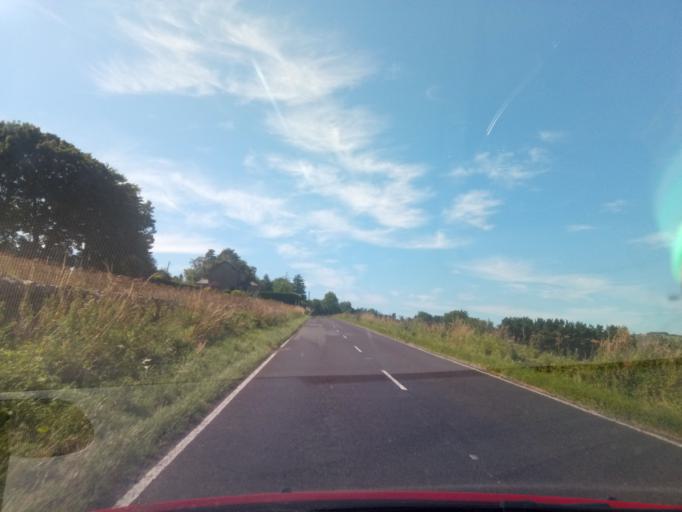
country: GB
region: England
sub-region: Northumberland
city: Bardon Mill
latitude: 54.9327
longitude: -2.3004
